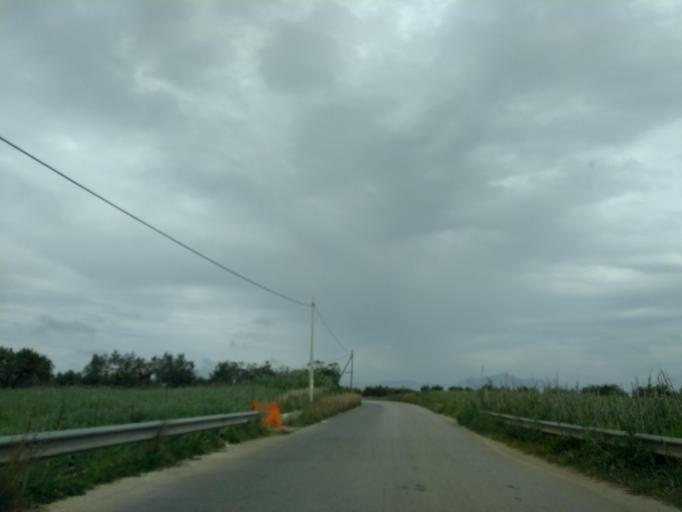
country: IT
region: Sicily
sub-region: Palermo
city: Partinico
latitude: 38.0067
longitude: 13.0682
